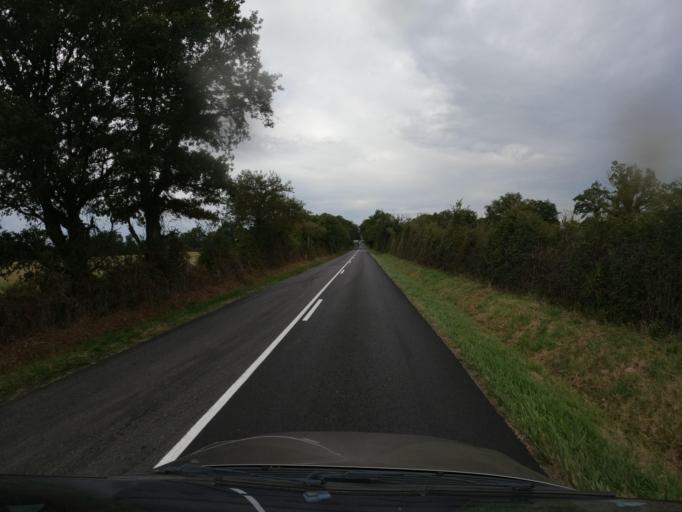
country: FR
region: Poitou-Charentes
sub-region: Departement de la Vienne
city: Saulge
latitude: 46.3439
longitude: 0.8283
